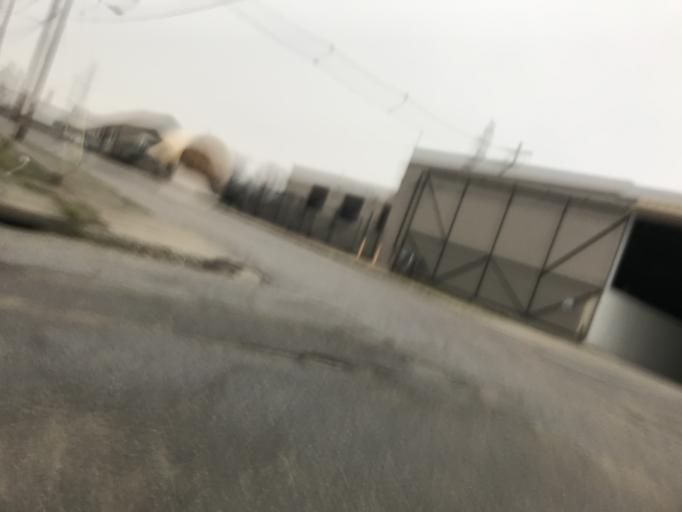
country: US
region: Indiana
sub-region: Clark County
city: Jeffersonville
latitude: 38.2568
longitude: -85.7333
